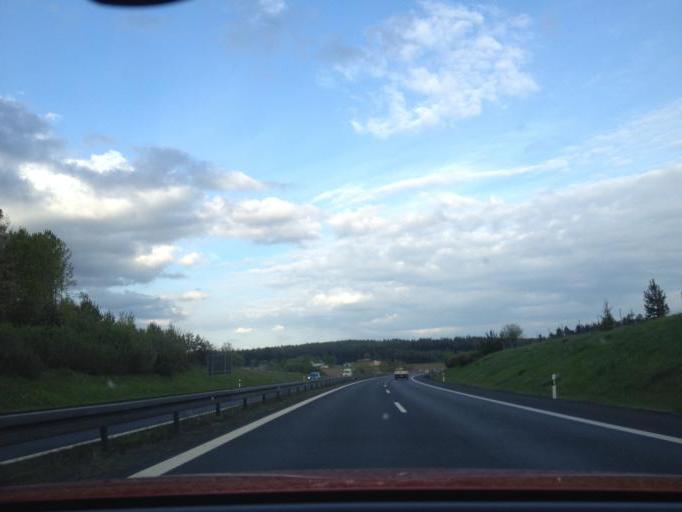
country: DE
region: Bavaria
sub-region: Upper Palatinate
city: Pechbrunn
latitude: 49.9798
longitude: 12.1639
